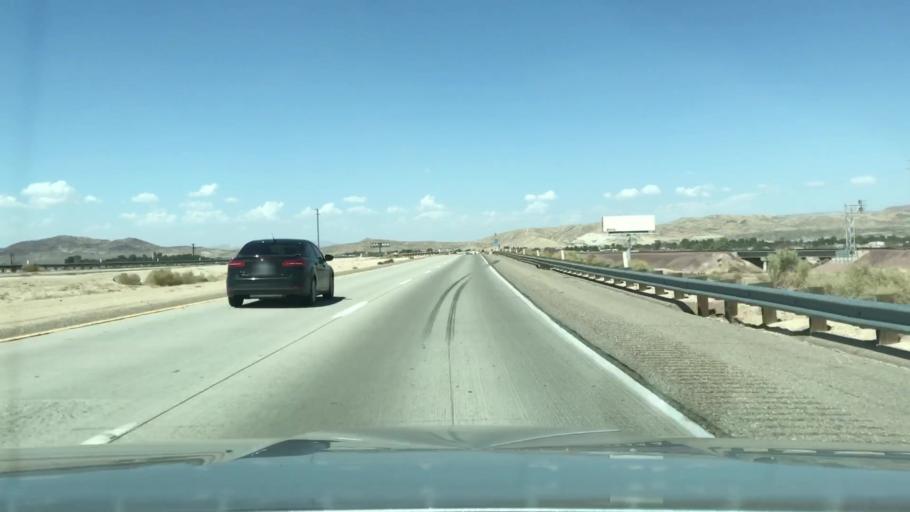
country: US
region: California
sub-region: San Bernardino County
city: Lenwood
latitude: 34.8904
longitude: -117.0936
